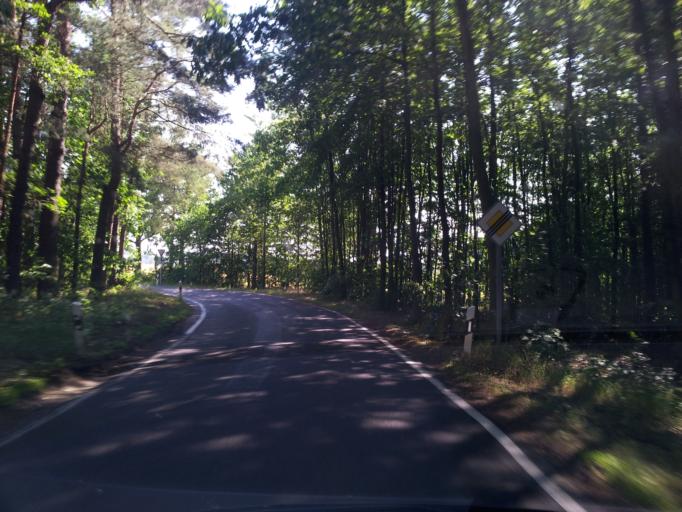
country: DE
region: Saxony
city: Hockendorf
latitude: 51.2345
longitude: 13.9071
